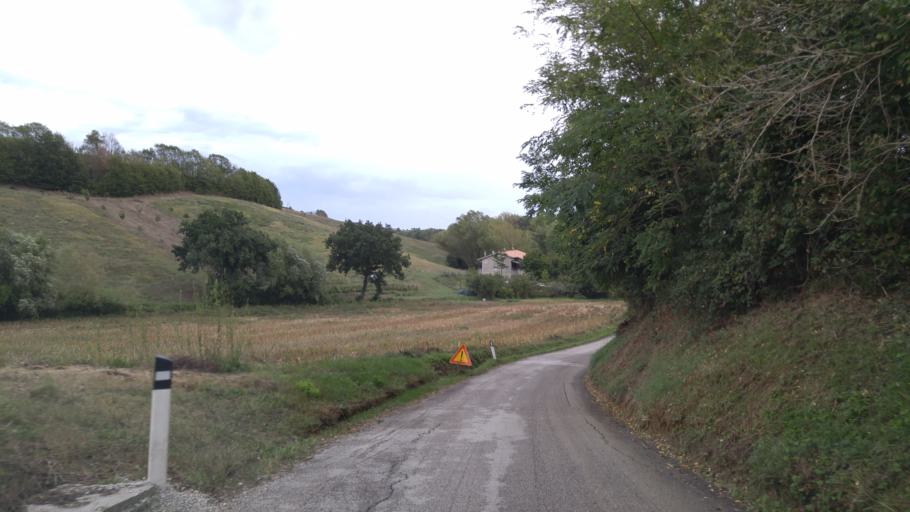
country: IT
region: The Marches
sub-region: Provincia di Pesaro e Urbino
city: Cartoceto
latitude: 43.7878
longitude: 12.8836
